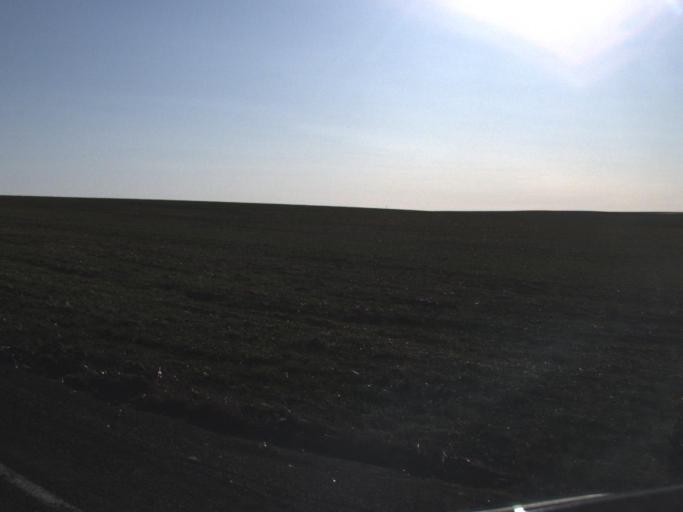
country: US
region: Washington
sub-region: Adams County
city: Ritzville
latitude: 47.0970
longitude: -118.3655
